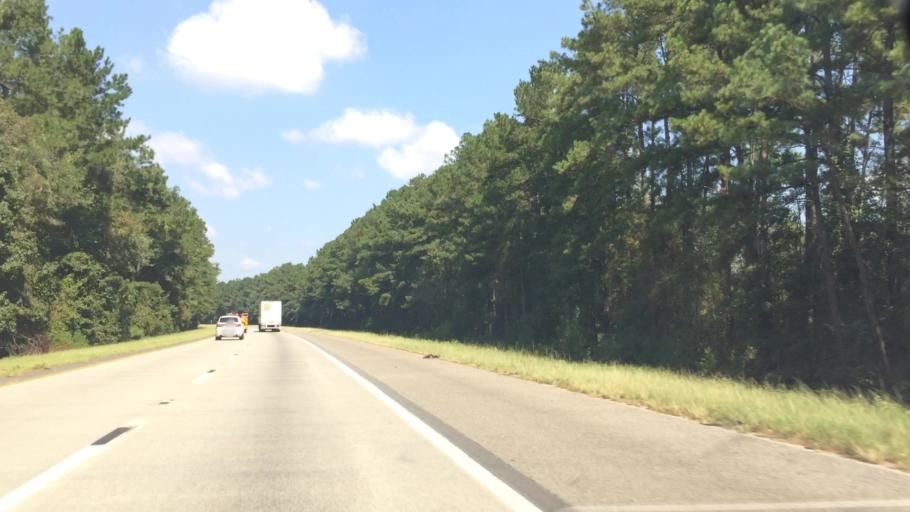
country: US
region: South Carolina
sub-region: Colleton County
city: Walterboro
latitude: 33.0194
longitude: -80.6654
